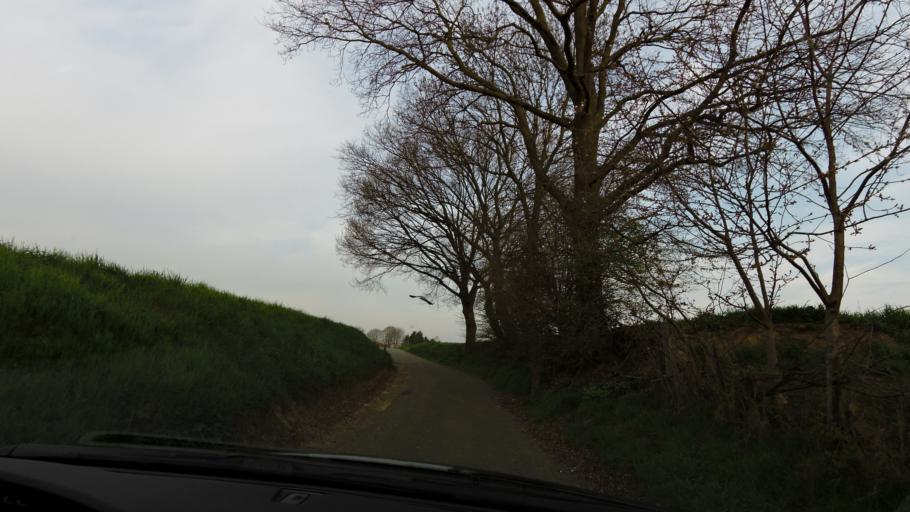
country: NL
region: Limburg
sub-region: Gemeente Onderbanken
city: Merkelbeek
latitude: 50.9698
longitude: 5.9467
